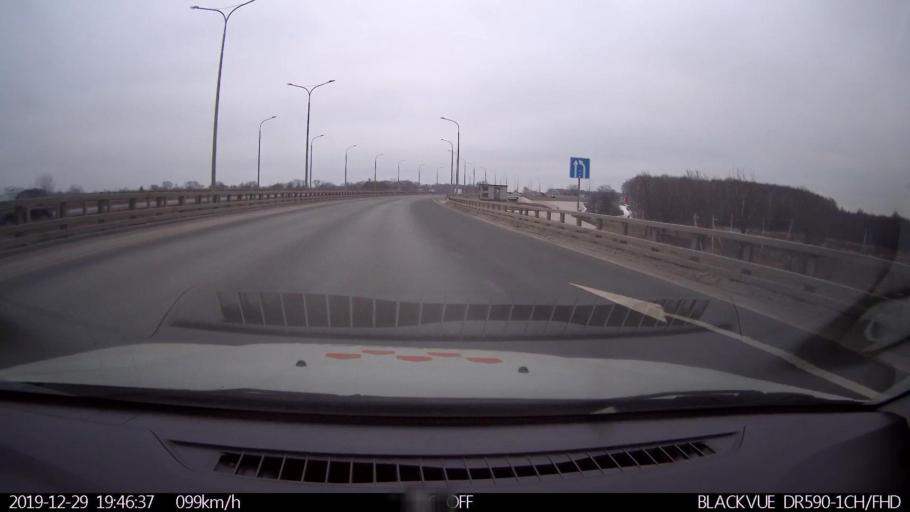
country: RU
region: Nizjnij Novgorod
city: Neklyudovo
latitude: 56.3968
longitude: 43.9916
